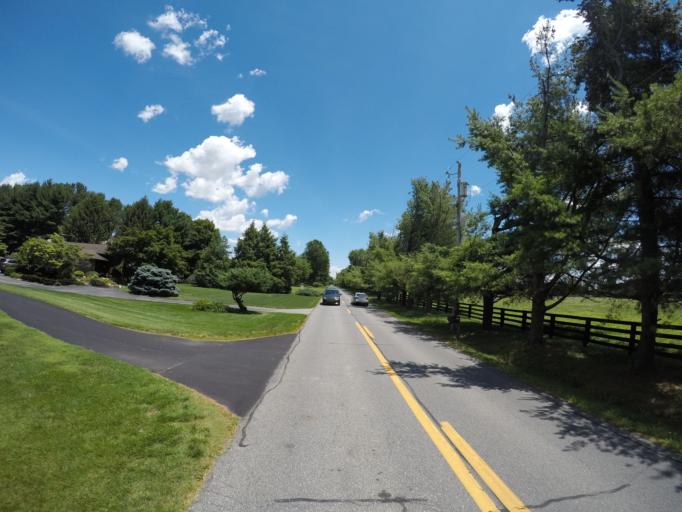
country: US
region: Delaware
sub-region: New Castle County
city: Middletown
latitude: 39.4810
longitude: -75.7465
